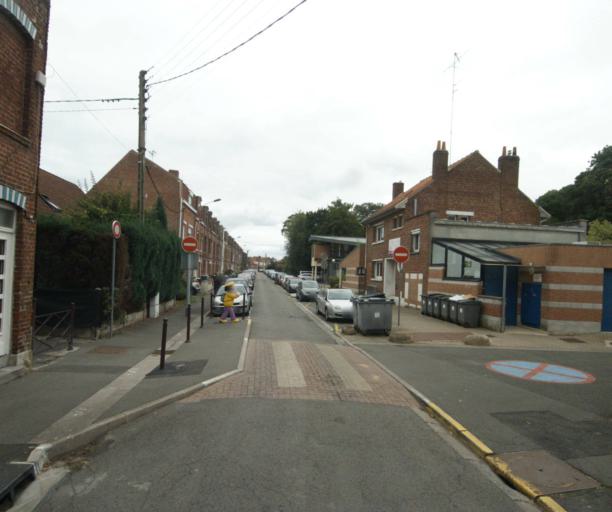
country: FR
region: Nord-Pas-de-Calais
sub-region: Departement du Nord
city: Lesquin
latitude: 50.5894
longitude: 3.1064
